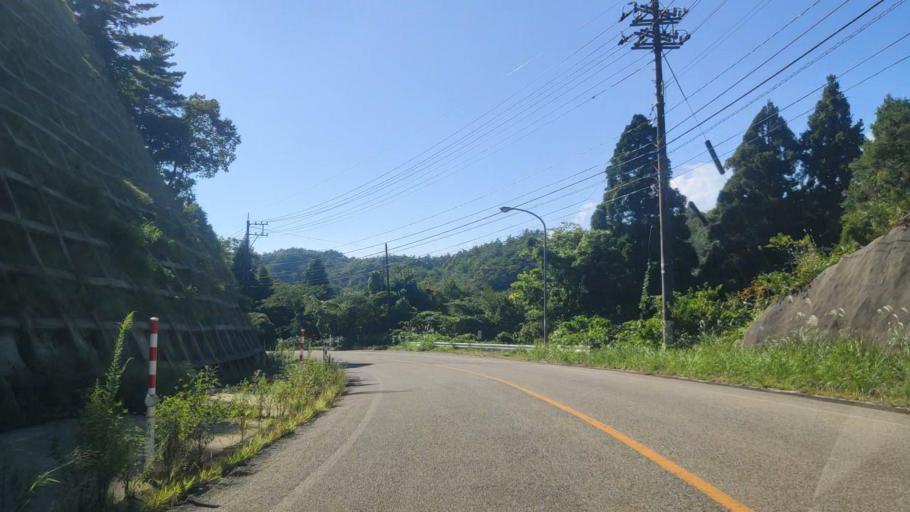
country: JP
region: Ishikawa
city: Nanao
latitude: 37.3164
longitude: 137.1604
